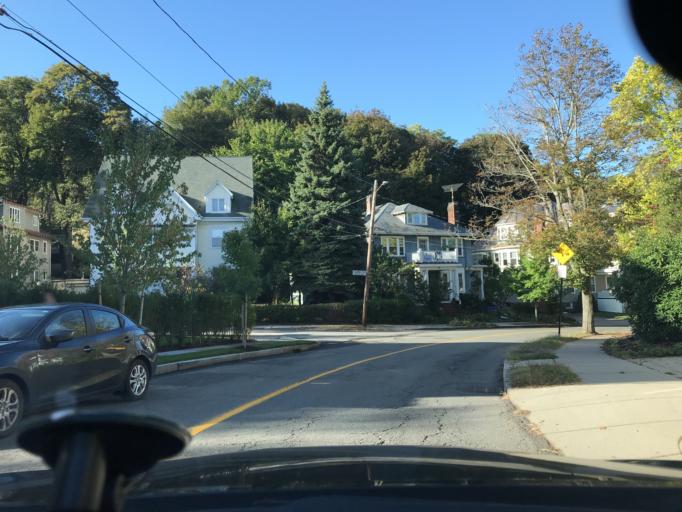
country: US
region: Massachusetts
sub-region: Norfolk County
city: Brookline
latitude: 42.3458
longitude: -71.1300
